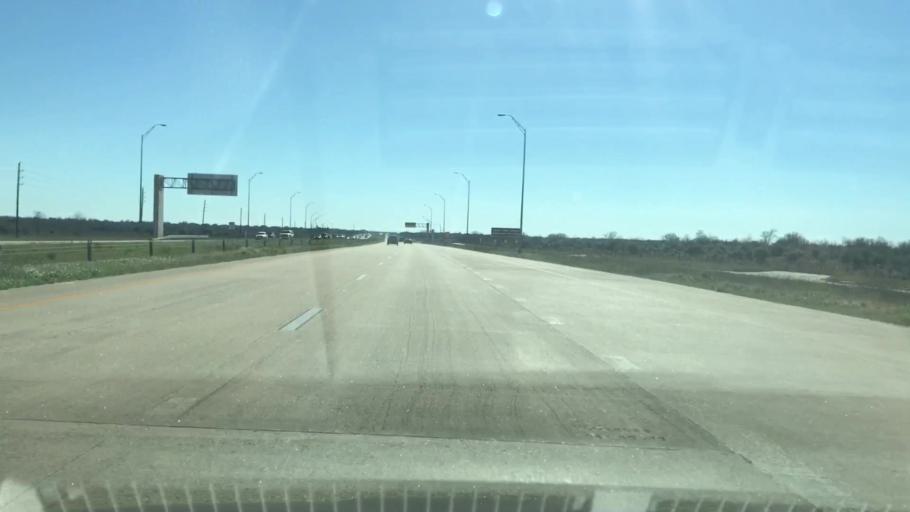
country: US
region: Texas
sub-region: Harris County
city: Cypress
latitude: 29.9865
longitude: -95.7696
